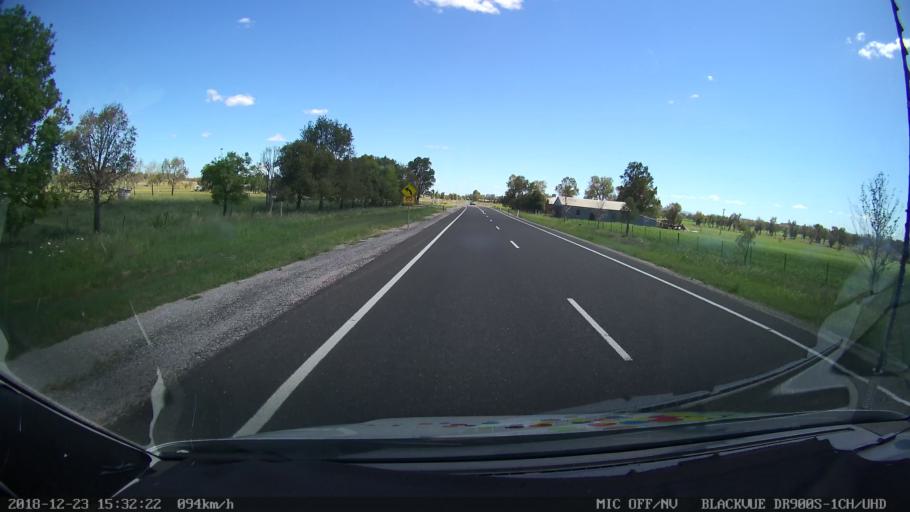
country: AU
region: New South Wales
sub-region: Tamworth Municipality
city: East Tamworth
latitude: -30.9847
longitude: 150.8702
